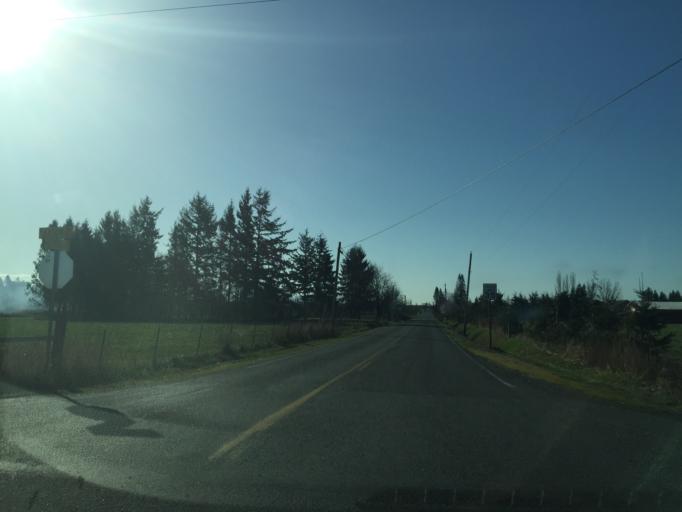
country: US
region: Washington
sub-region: Whatcom County
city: Marietta-Alderwood
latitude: 48.8480
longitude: -122.5191
